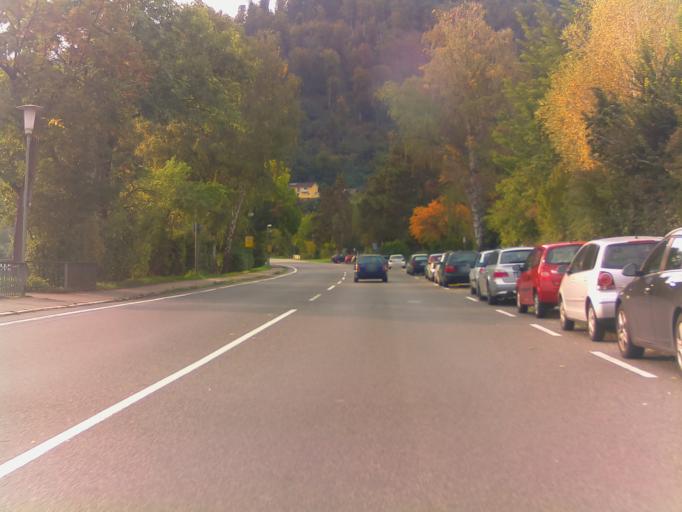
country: DE
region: Baden-Wuerttemberg
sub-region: Karlsruhe Region
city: Eberbach
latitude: 49.4632
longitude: 8.9812
